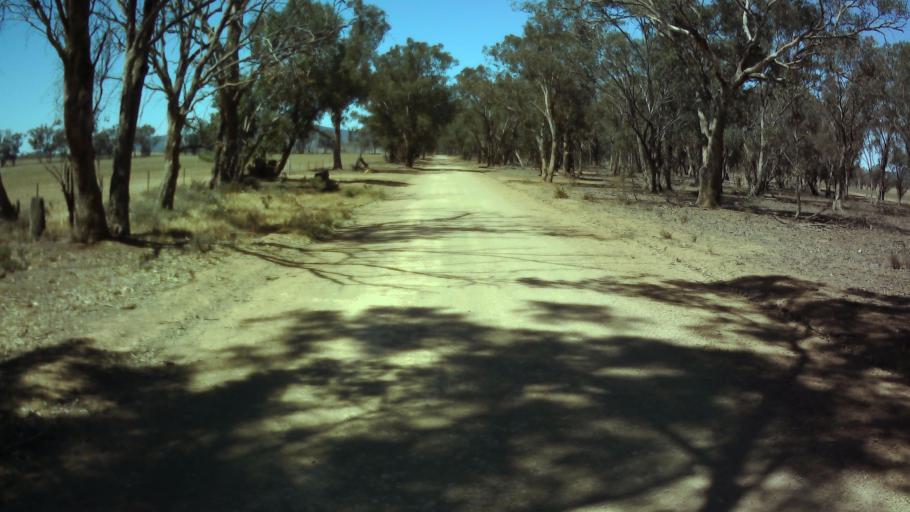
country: AU
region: New South Wales
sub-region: Weddin
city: Grenfell
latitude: -33.9022
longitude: 148.0823
